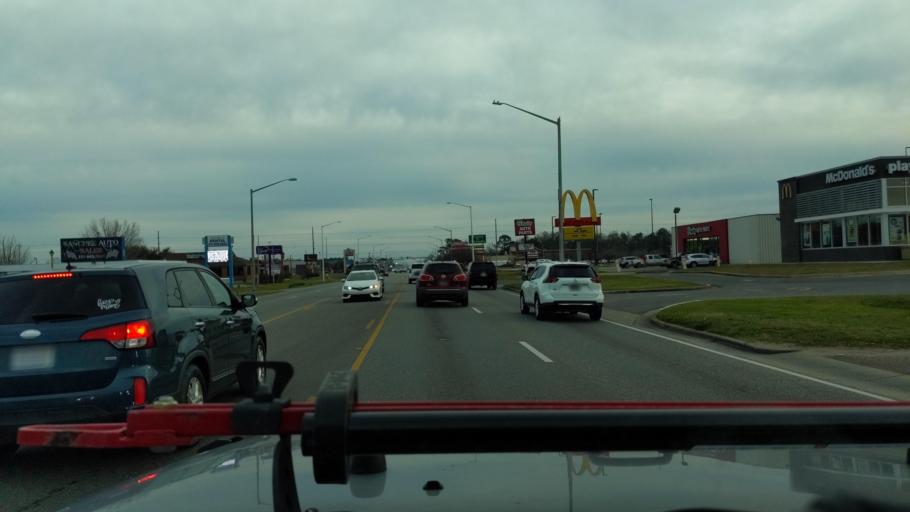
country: US
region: Alabama
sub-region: Baldwin County
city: Foley
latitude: 30.3956
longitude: -87.6834
